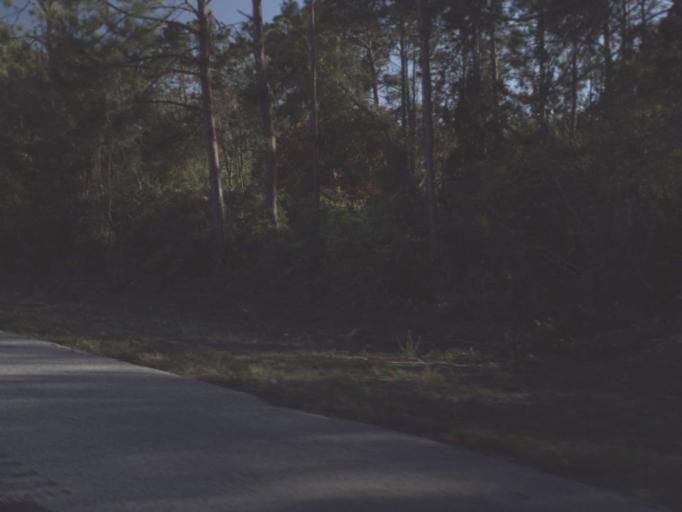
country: US
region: Florida
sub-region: Flagler County
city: Palm Coast
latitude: 29.5304
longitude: -81.2047
